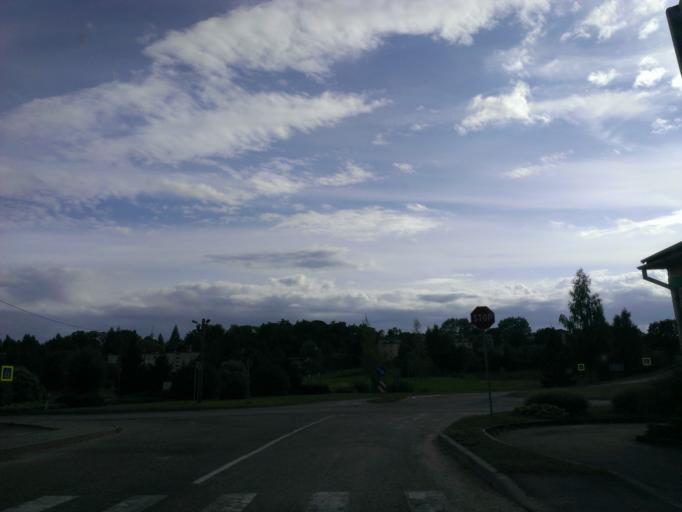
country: LV
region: Malpils
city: Malpils
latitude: 56.8941
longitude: 25.1815
